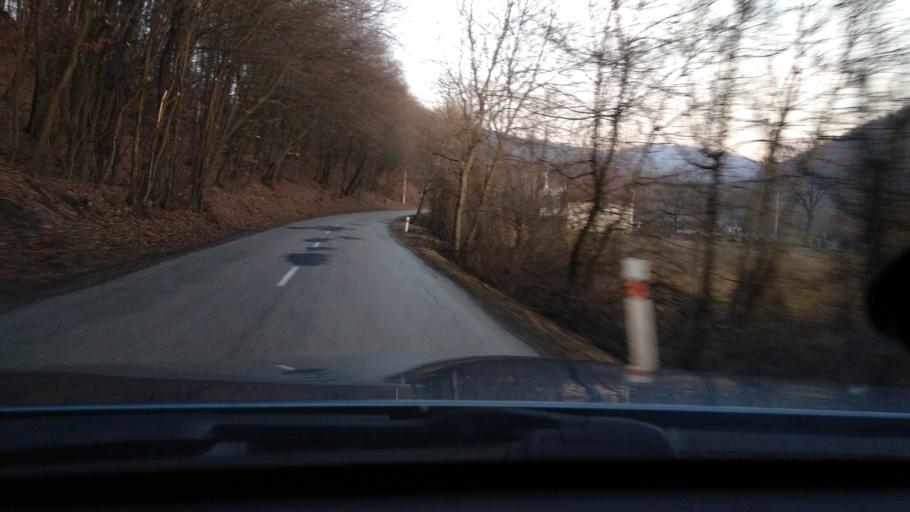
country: SK
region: Nitriansky
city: Trencianske Teplice
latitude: 48.8427
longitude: 18.2367
